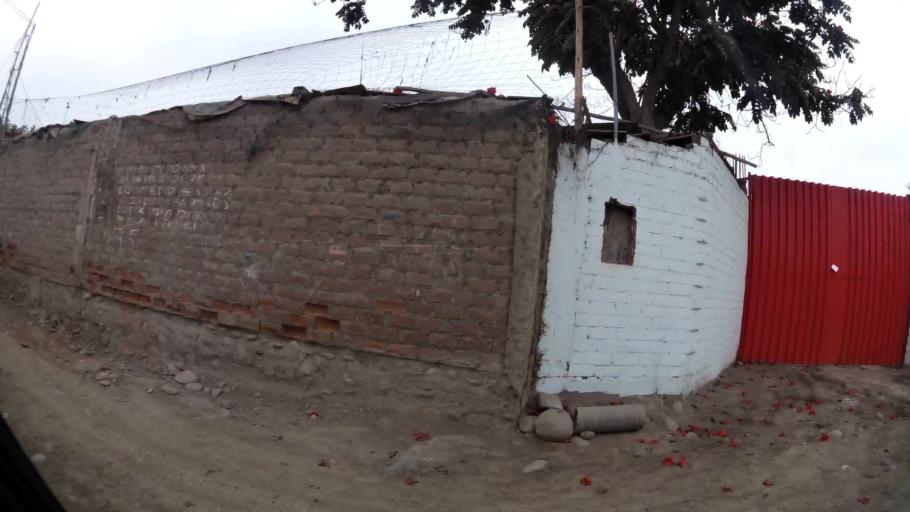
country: PE
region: Lima
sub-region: Lima
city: Urb. Santo Domingo
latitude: -11.8963
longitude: -77.0602
